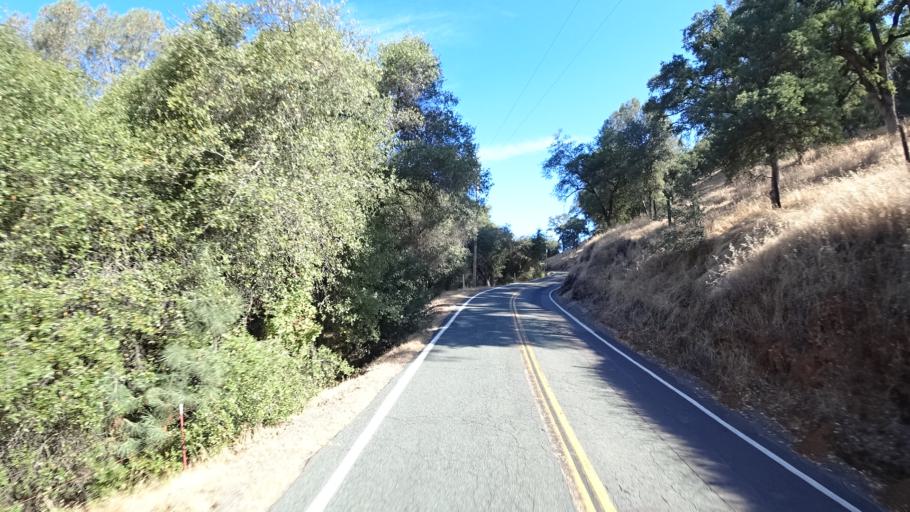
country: US
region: California
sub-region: Calaveras County
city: San Andreas
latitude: 38.1599
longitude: -120.6127
